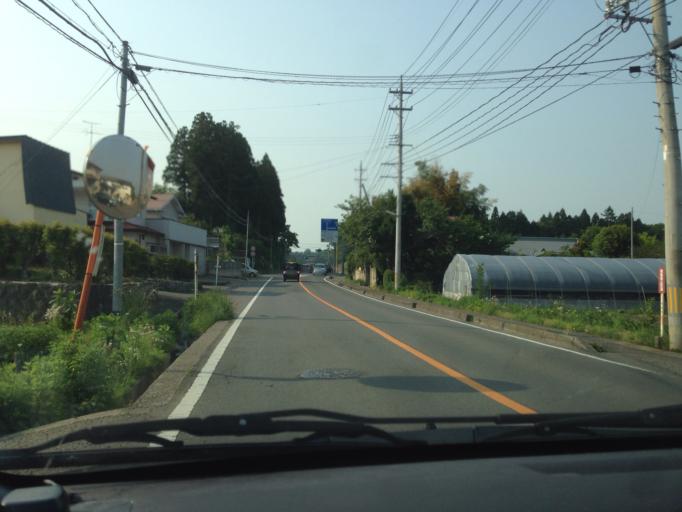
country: JP
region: Tochigi
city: Kuroiso
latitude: 37.0986
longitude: 140.1973
